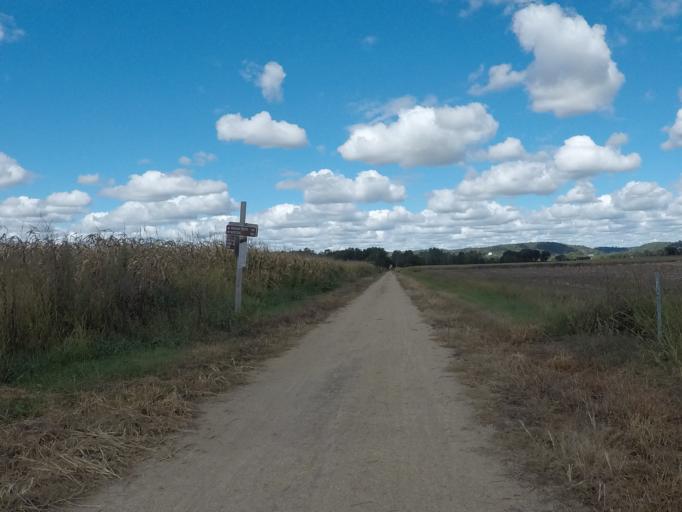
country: US
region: Wisconsin
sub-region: Richland County
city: Richland Center
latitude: 43.2969
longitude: -90.3318
